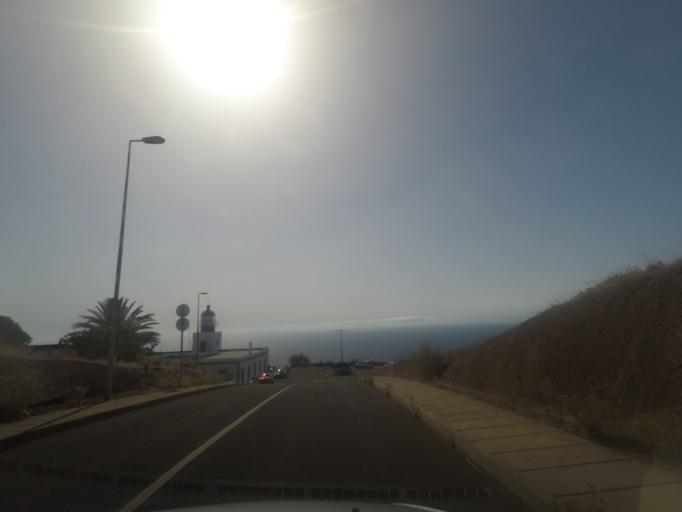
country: PT
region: Madeira
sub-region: Calheta
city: Faja da Ovelha
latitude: 32.8140
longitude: -17.2621
